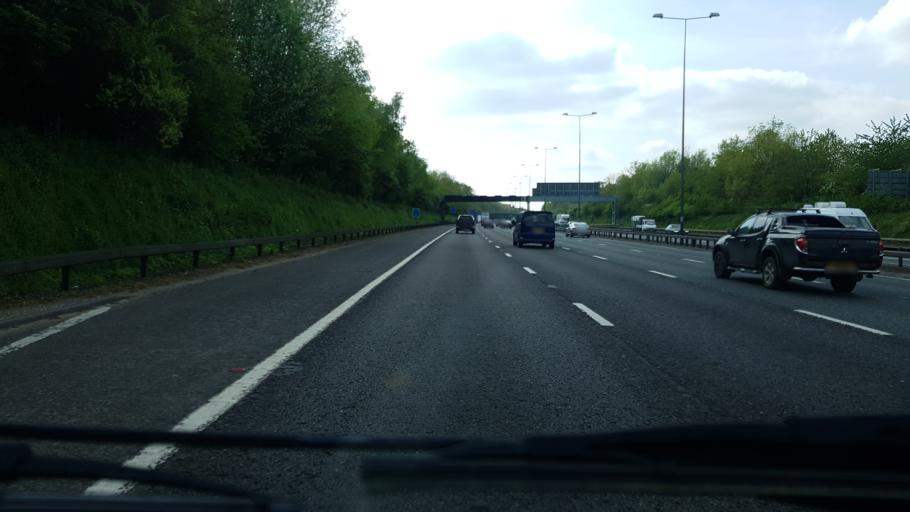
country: GB
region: England
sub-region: Surrey
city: Reigate
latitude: 51.2576
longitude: -0.2064
